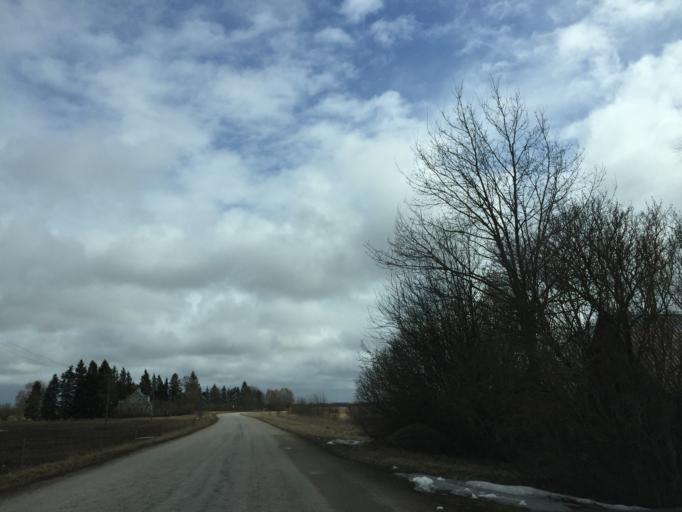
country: EE
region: Laeaene
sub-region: Lihula vald
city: Lihula
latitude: 58.7327
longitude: 23.8689
